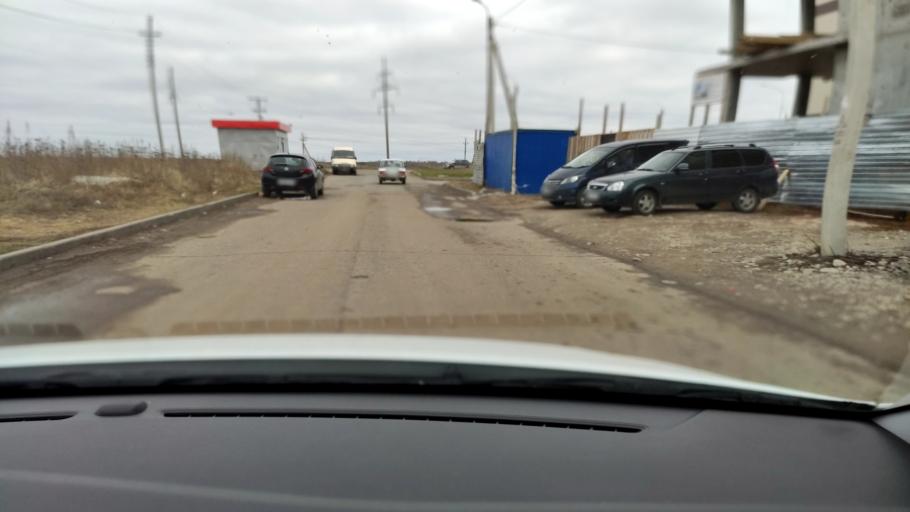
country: RU
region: Tatarstan
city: Osinovo
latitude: 55.8726
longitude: 48.8770
